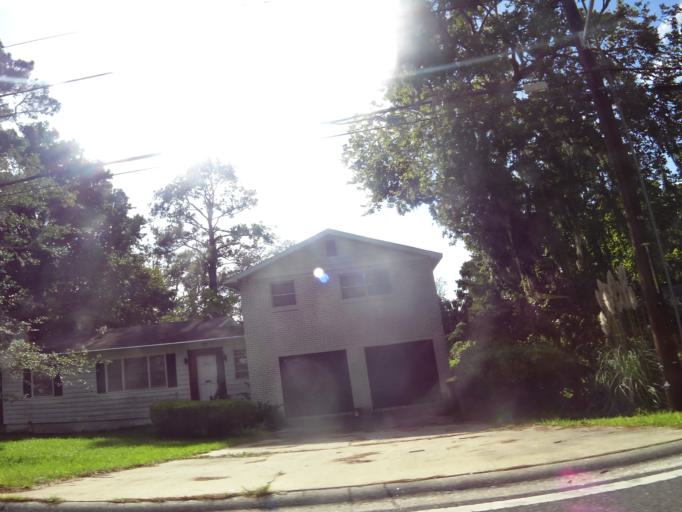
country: US
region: Florida
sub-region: Duval County
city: Jacksonville
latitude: 30.2859
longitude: -81.7388
